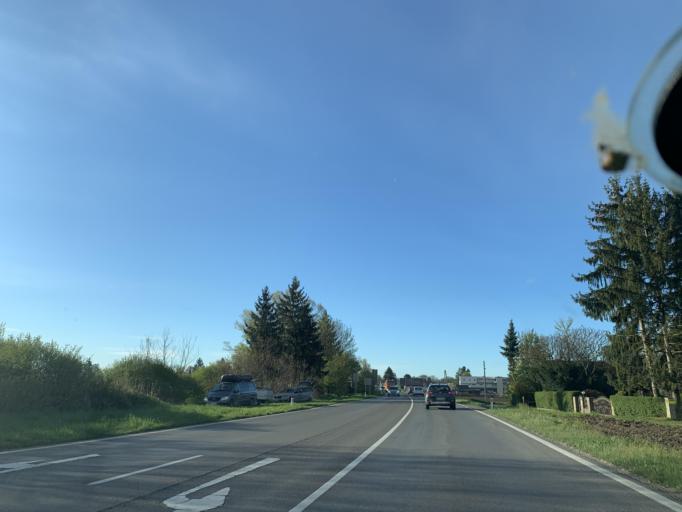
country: AT
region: Styria
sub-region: Politischer Bezirk Leibnitz
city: Kaindorf an der Sulm
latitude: 46.8124
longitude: 15.5268
